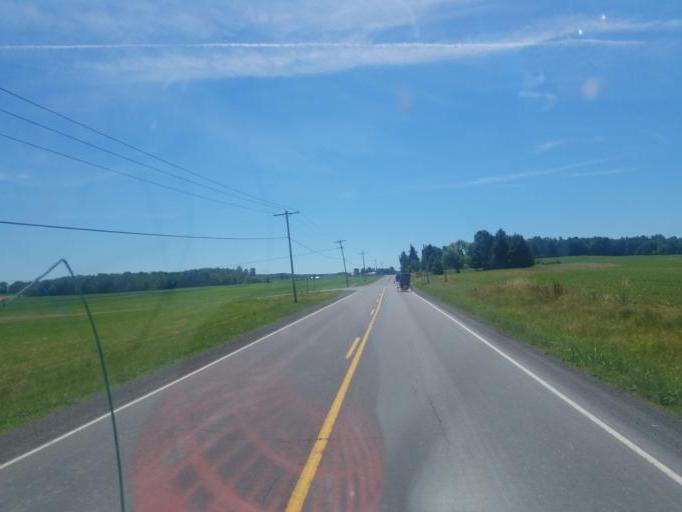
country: US
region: New York
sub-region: Yates County
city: Penn Yan
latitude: 42.6235
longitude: -76.9987
